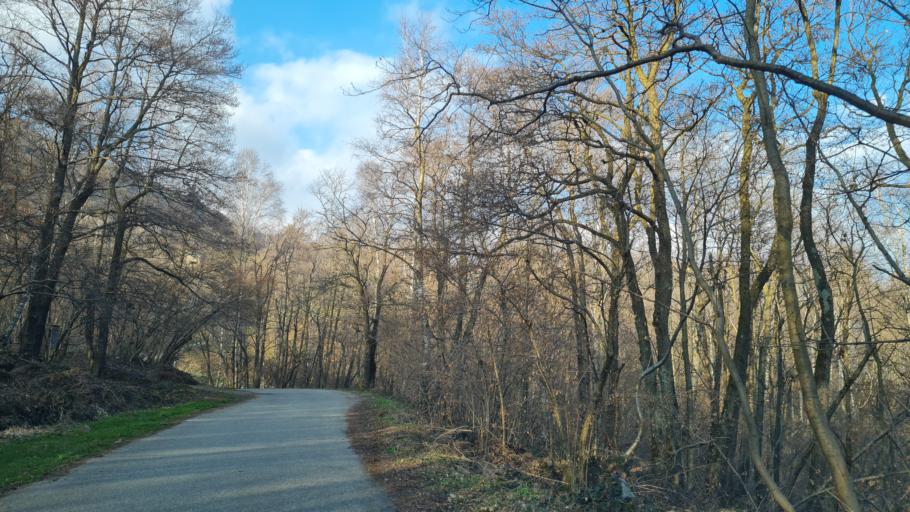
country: IT
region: Piedmont
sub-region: Provincia di Biella
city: Donato
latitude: 45.5474
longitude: 7.9175
